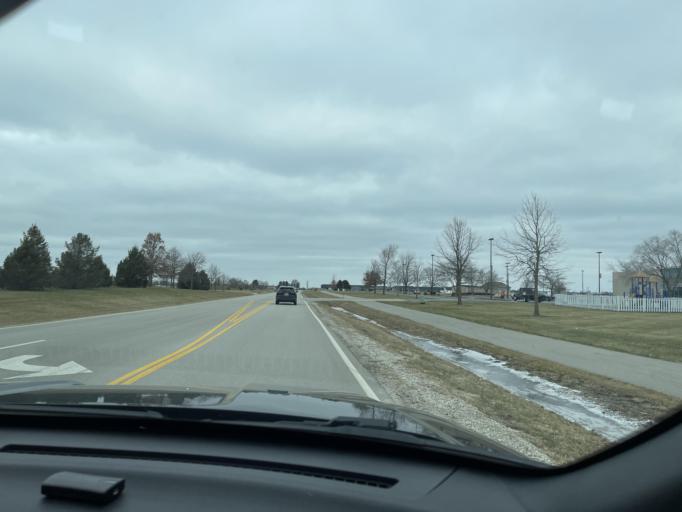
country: US
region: Illinois
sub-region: Sangamon County
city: Jerome
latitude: 39.7566
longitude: -89.7531
